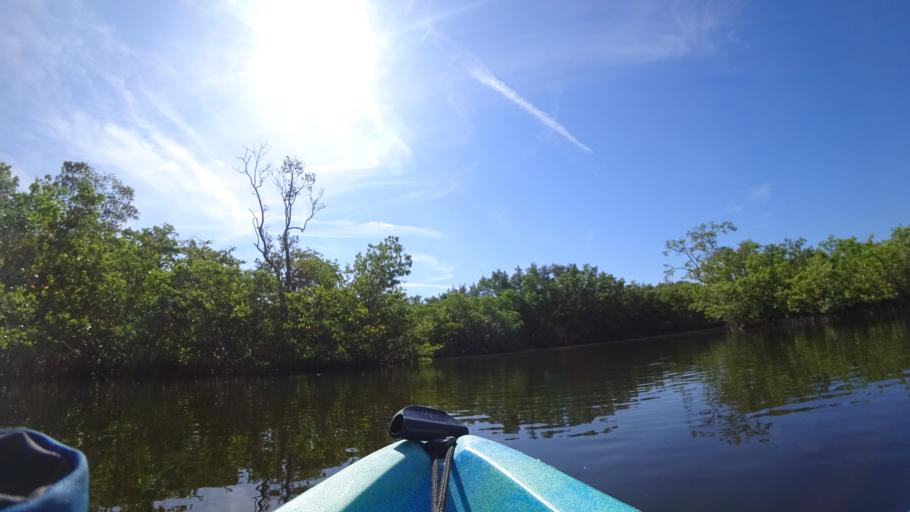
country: US
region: Florida
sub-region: Manatee County
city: West Bradenton
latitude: 27.5159
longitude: -82.6620
